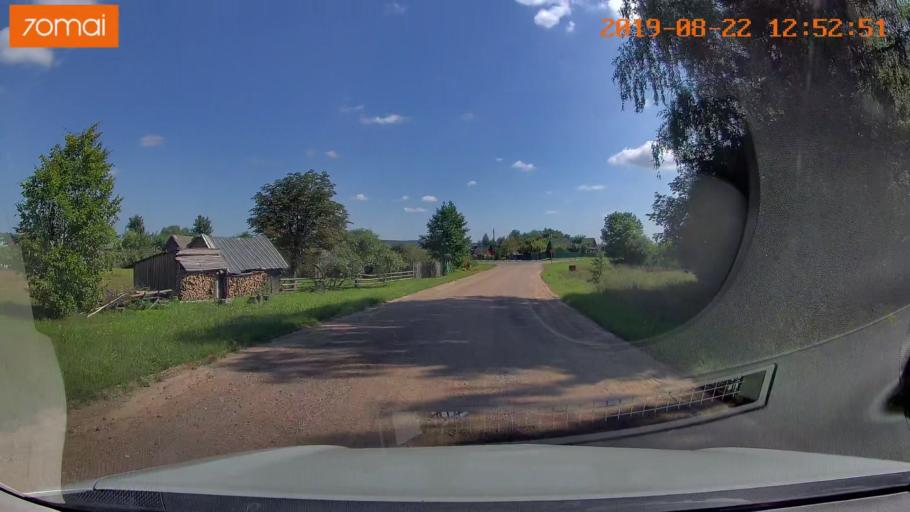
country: BY
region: Minsk
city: Prawdzinski
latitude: 53.4508
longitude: 27.6806
